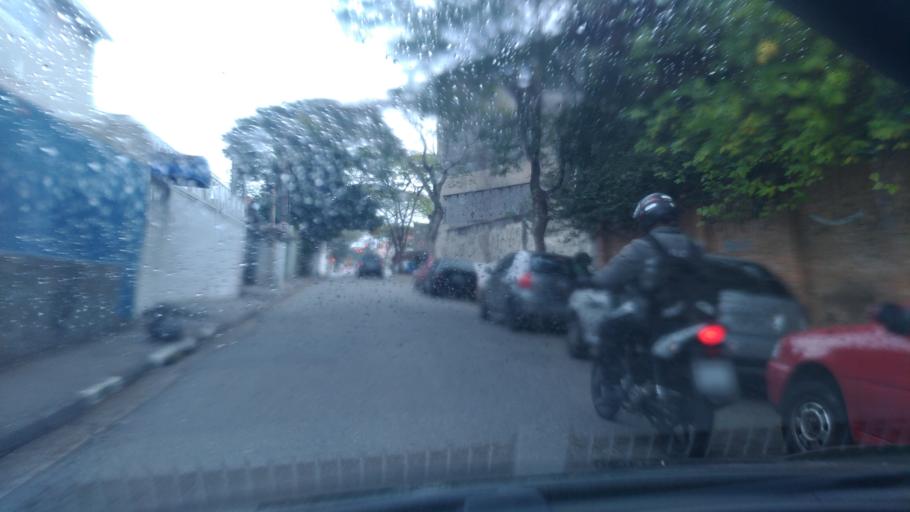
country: BR
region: Sao Paulo
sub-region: Sao Bernardo Do Campo
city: Sao Bernardo do Campo
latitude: -23.6907
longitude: -46.5558
